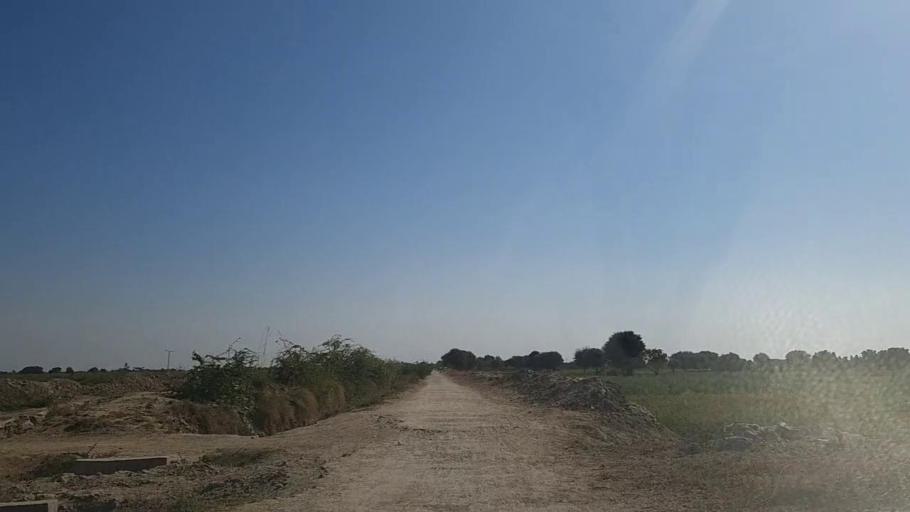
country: PK
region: Sindh
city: Samaro
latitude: 25.2420
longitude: 69.4837
